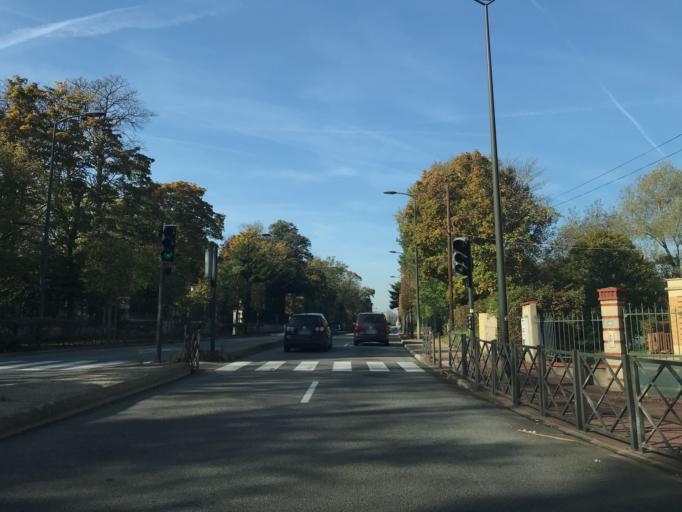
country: FR
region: Ile-de-France
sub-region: Departement des Yvelines
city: Fourqueux
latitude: 48.8996
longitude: 2.0678
